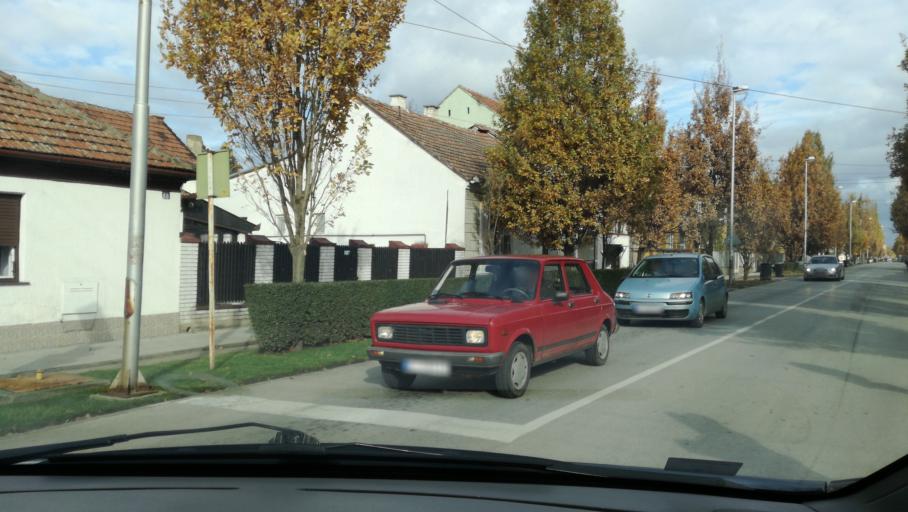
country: RS
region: Autonomna Pokrajina Vojvodina
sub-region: Severnobanatski Okrug
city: Kikinda
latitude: 45.8281
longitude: 20.4580
